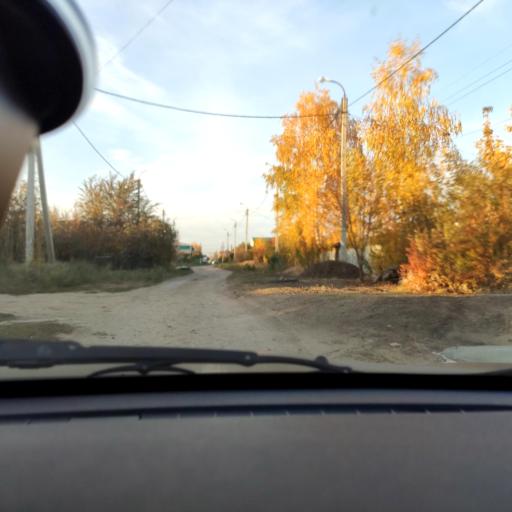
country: RU
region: Samara
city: Tol'yatti
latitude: 53.5335
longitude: 49.3908
